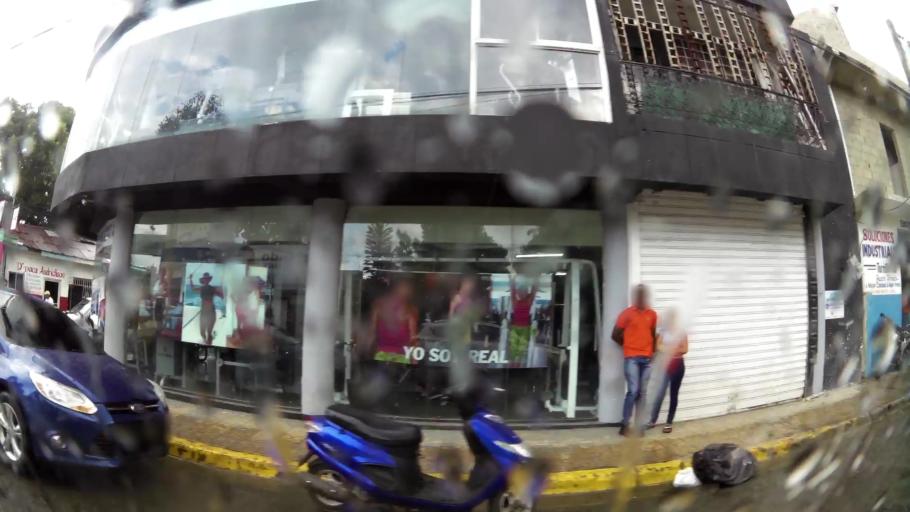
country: DO
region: Monsenor Nouel
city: Bonao
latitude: 18.9448
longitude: -70.4100
